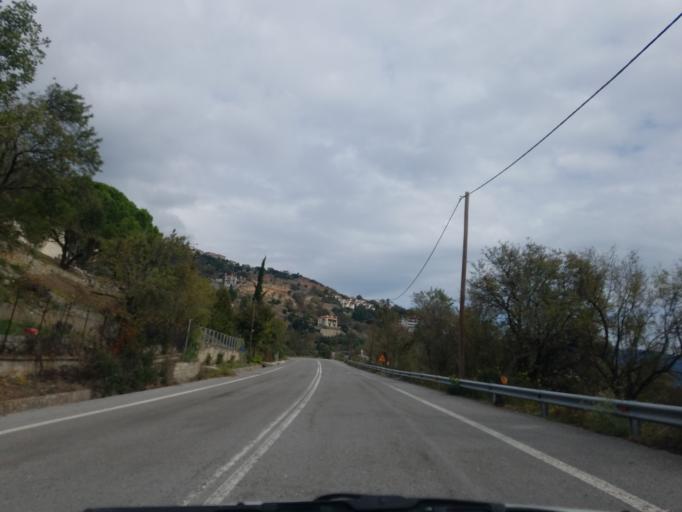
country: GR
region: Central Greece
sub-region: Nomos Voiotias
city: Arachova
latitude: 38.4856
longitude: 22.5663
